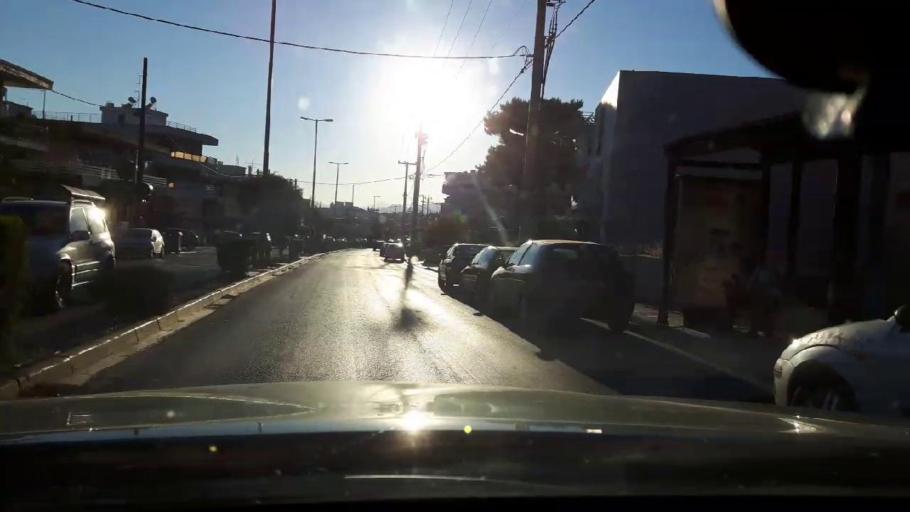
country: GR
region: Attica
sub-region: Nomarchia Athinas
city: Melissia
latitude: 38.0517
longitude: 23.8307
